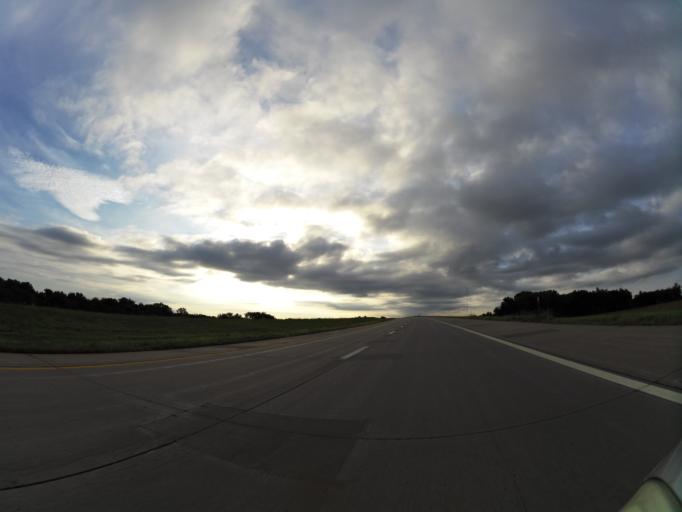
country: US
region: Kansas
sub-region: Reno County
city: Haven
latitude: 37.8744
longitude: -97.6951
